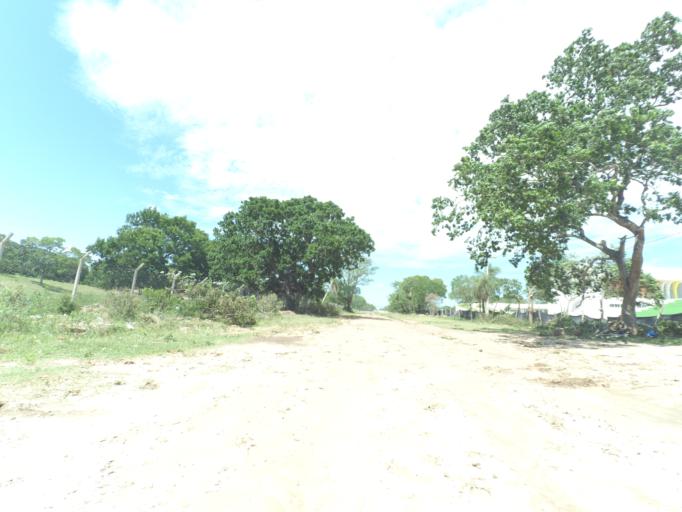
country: BO
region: Santa Cruz
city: Santa Cruz de la Sierra
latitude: -17.8138
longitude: -63.2362
